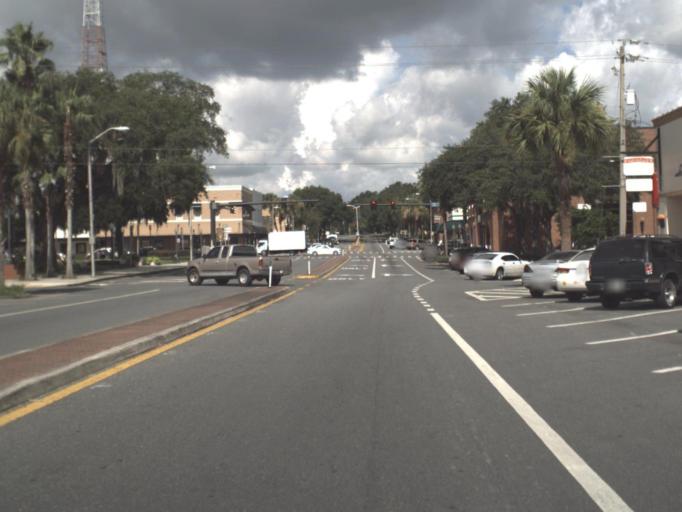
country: US
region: Florida
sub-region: Pasco County
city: Dade City
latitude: 28.3646
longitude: -82.1878
